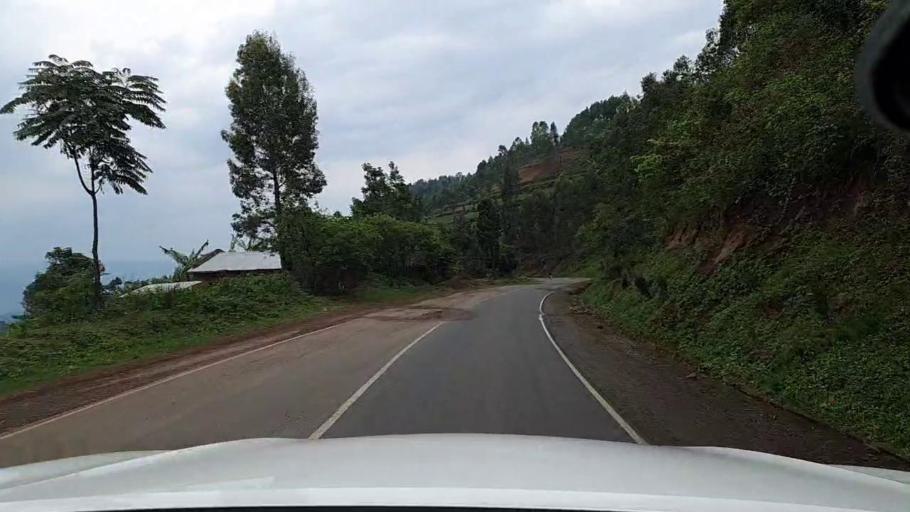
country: RW
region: Western Province
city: Cyangugu
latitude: -2.6499
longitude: 28.9668
